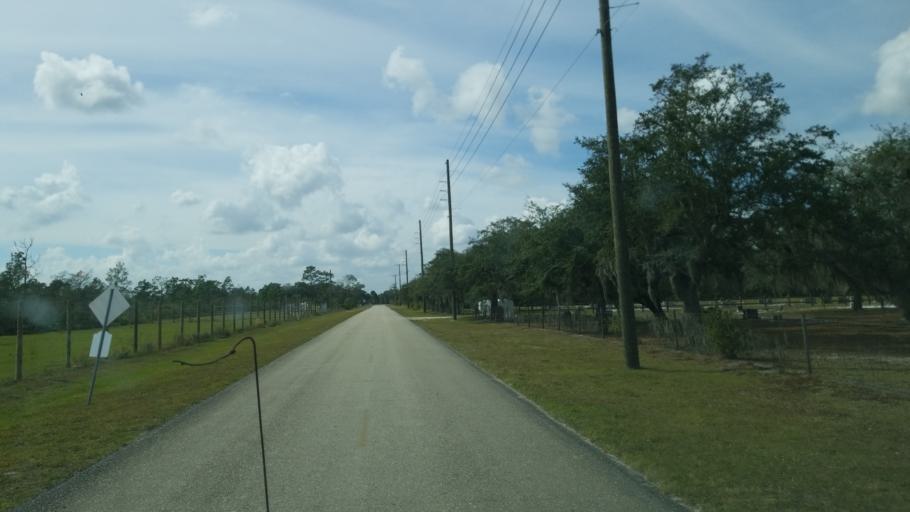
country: US
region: Florida
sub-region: Okeechobee County
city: Cypress Quarters
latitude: 27.5232
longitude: -80.8017
